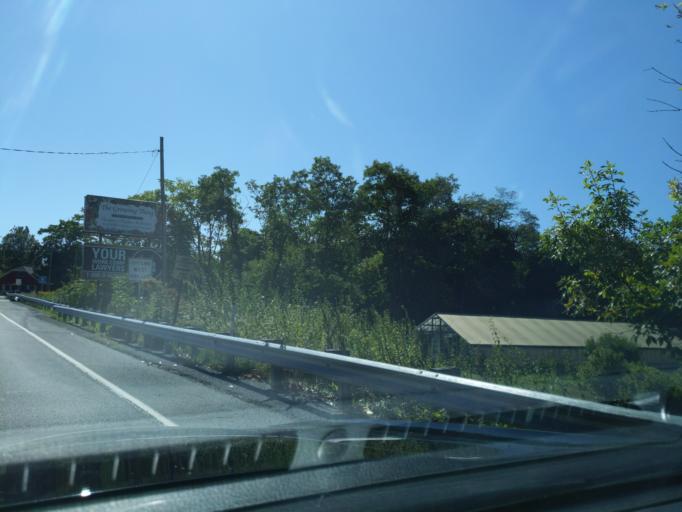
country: US
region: Pennsylvania
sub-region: Blair County
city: Greenwood
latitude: 40.5289
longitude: -78.3635
